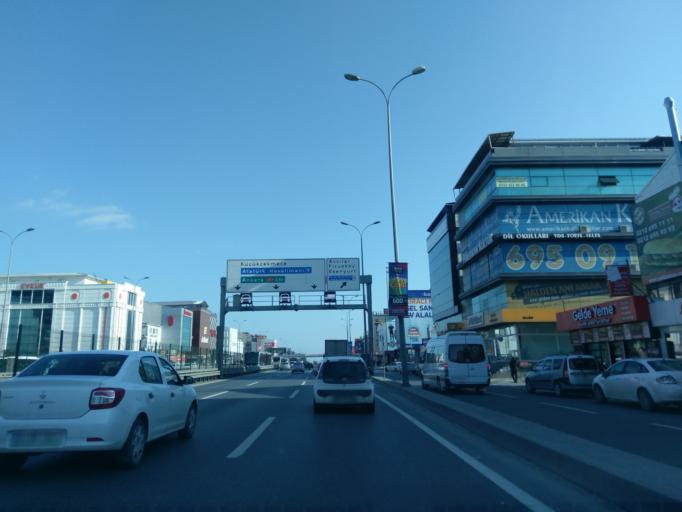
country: TR
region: Istanbul
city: Yakuplu
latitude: 40.9904
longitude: 28.7139
